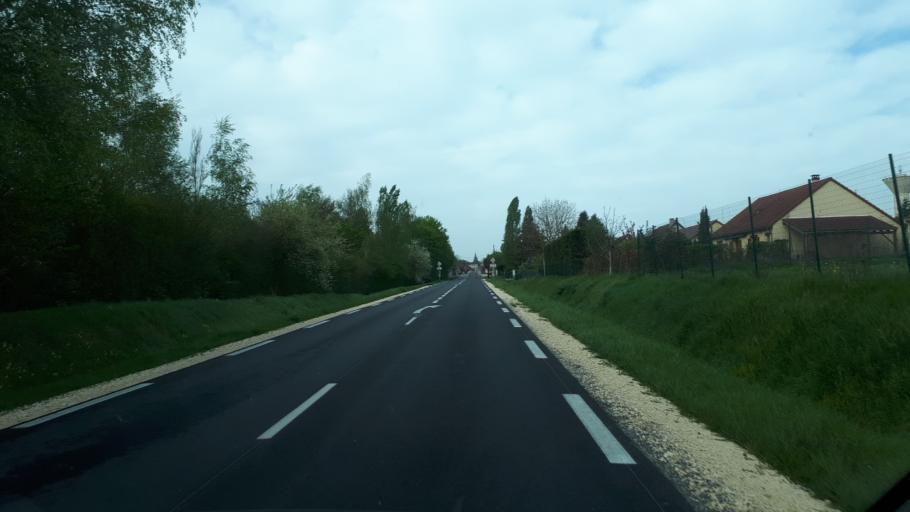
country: FR
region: Centre
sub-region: Departement du Cher
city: Rians
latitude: 47.2032
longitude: 2.5841
